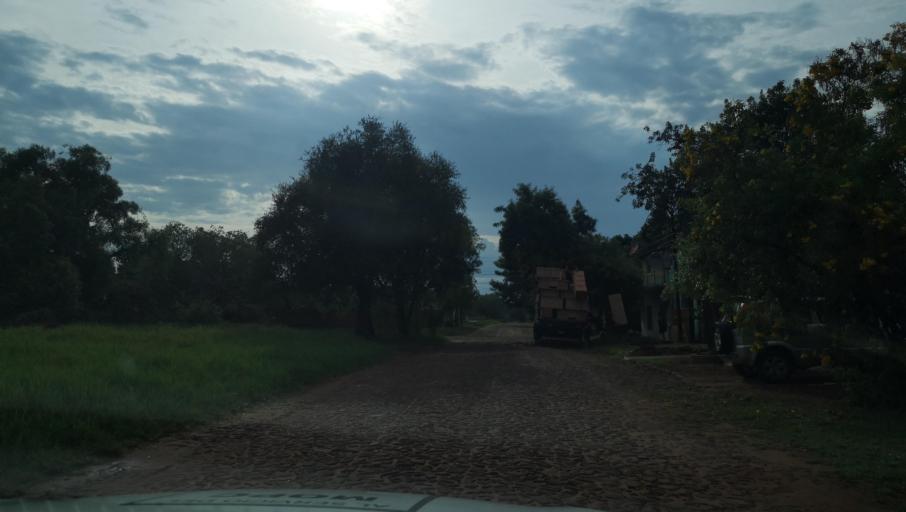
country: PY
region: Misiones
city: Santa Maria
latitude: -26.8815
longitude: -57.0306
